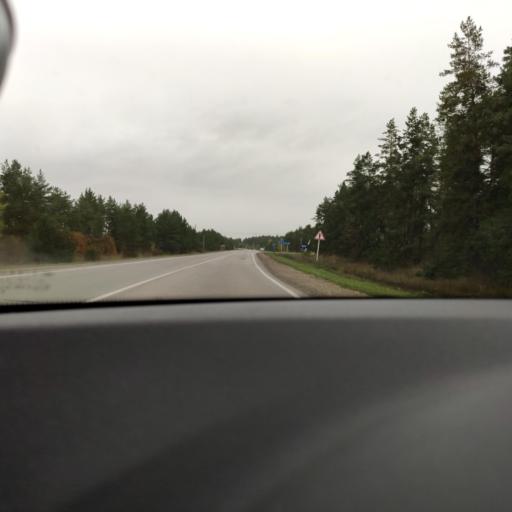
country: RU
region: Samara
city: Mirnyy
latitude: 53.5310
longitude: 50.3049
